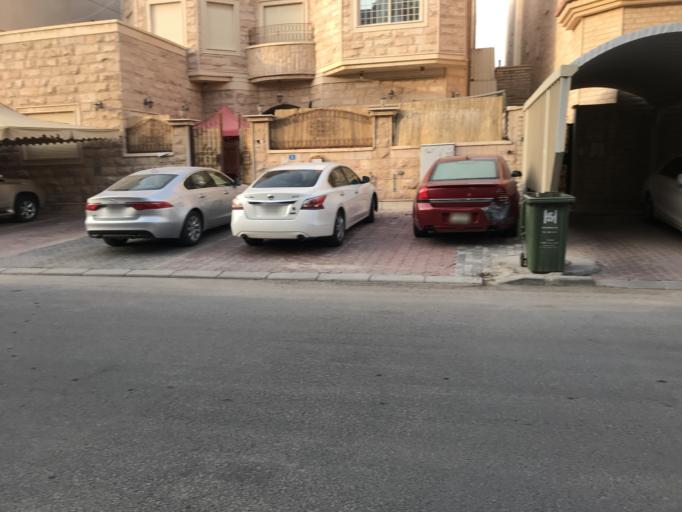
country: KW
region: Al Asimah
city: Ar Rabiyah
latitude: 29.2440
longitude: 47.9064
